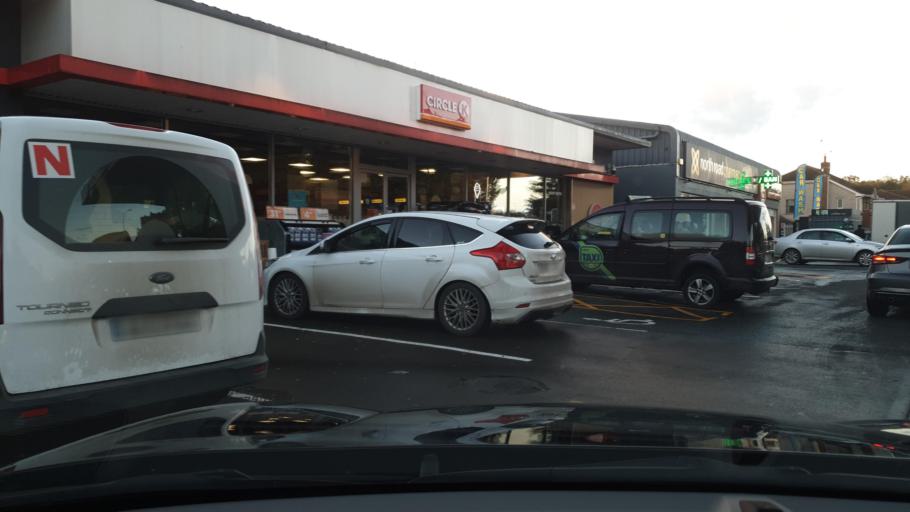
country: IE
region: Leinster
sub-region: Lu
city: Drogheda
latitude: 53.7237
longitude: -6.3631
